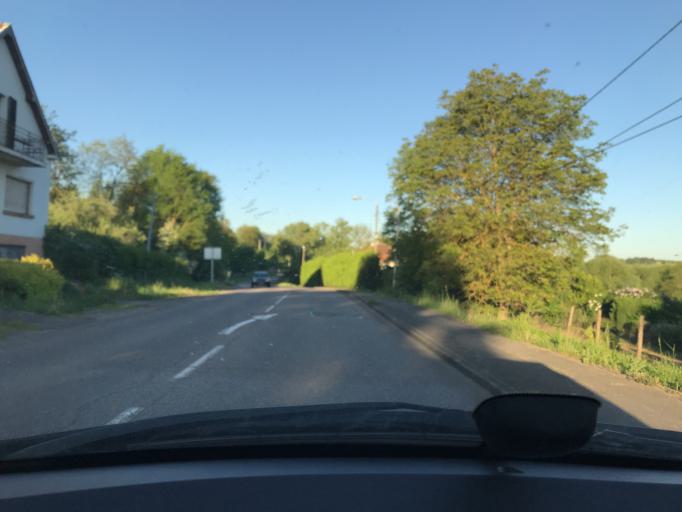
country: FR
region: Lorraine
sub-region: Departement de la Moselle
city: Sarreguemines
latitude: 49.1098
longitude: 7.0374
